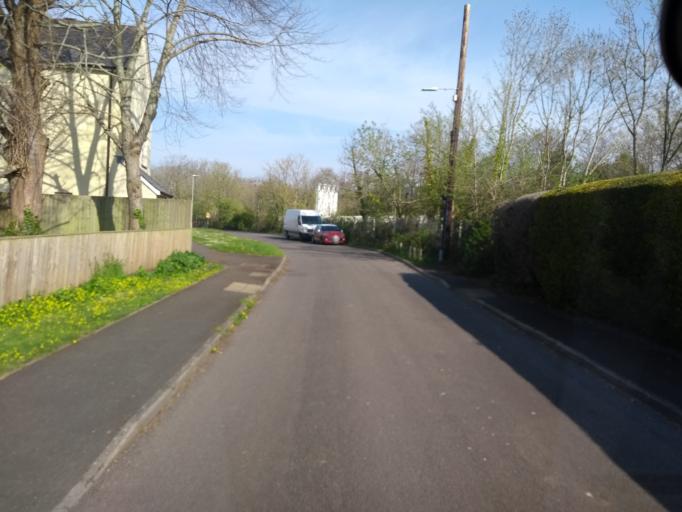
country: GB
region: England
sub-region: Somerset
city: Creech Saint Michael
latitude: 50.9783
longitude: -2.9915
